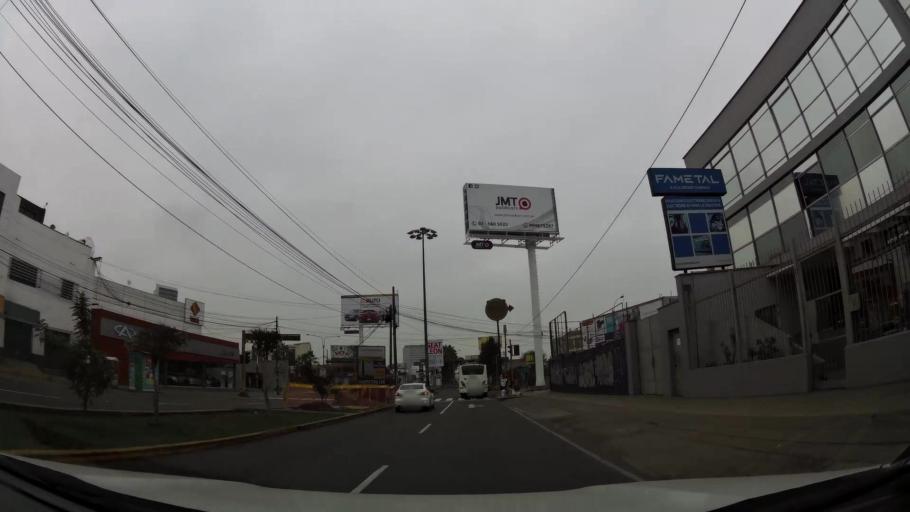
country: PE
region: Lima
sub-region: Lima
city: San Isidro
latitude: -12.1039
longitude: -77.0187
